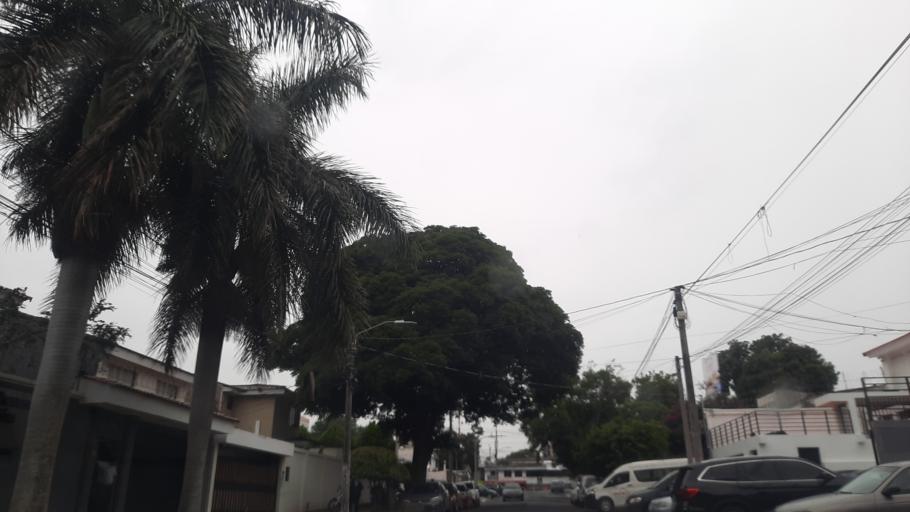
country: SV
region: La Libertad
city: Antiguo Cuscatlan
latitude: 13.6894
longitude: -89.2379
